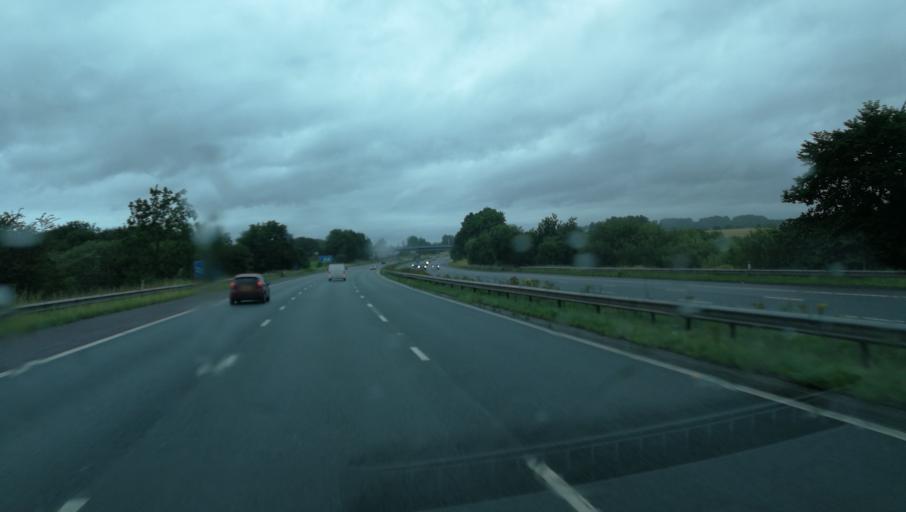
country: GB
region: England
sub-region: Borough of Bolton
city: Blackrod
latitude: 53.5946
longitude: -2.5689
